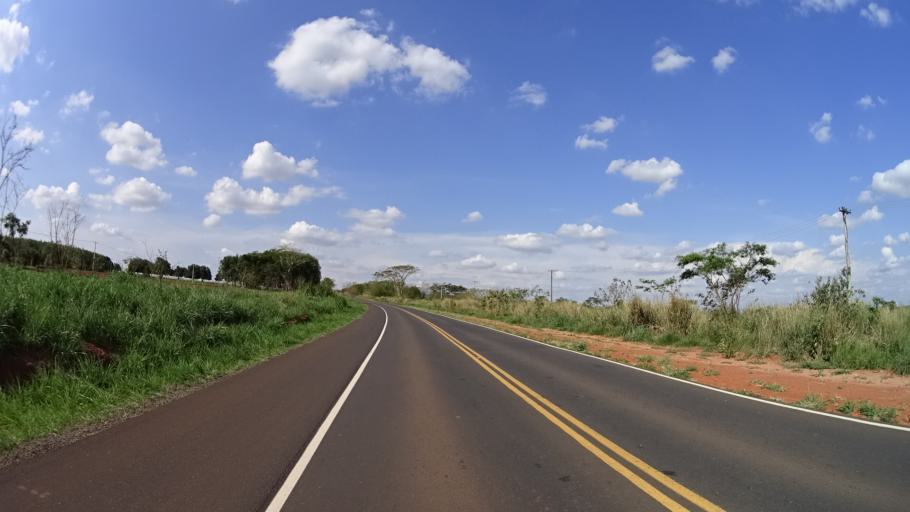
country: BR
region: Sao Paulo
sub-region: Guapiacu
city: Guapiacu
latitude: -21.0046
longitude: -49.2156
